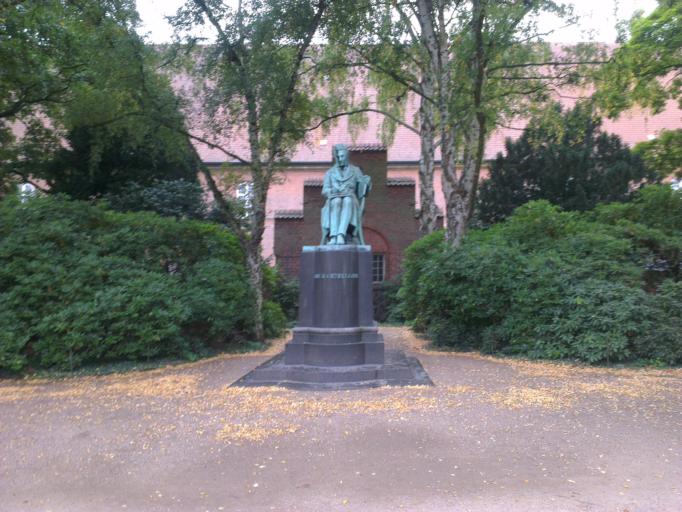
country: DK
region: Capital Region
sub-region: Kobenhavn
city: Christianshavn
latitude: 55.6745
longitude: 12.5811
